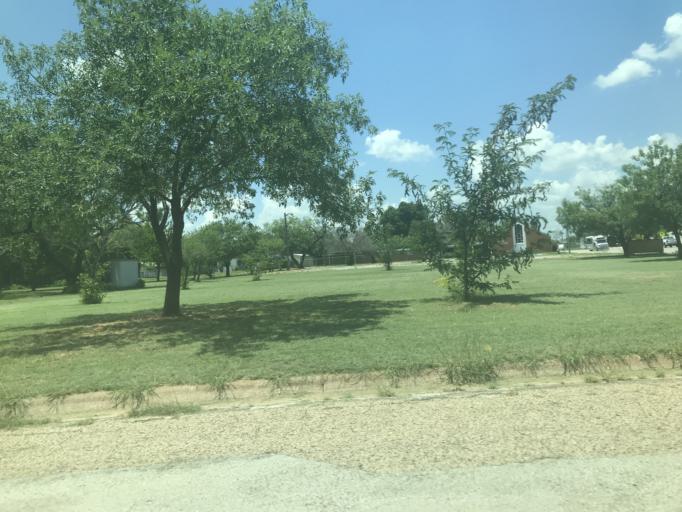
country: US
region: Texas
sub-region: Taylor County
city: Abilene
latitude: 32.4741
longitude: -99.7503
